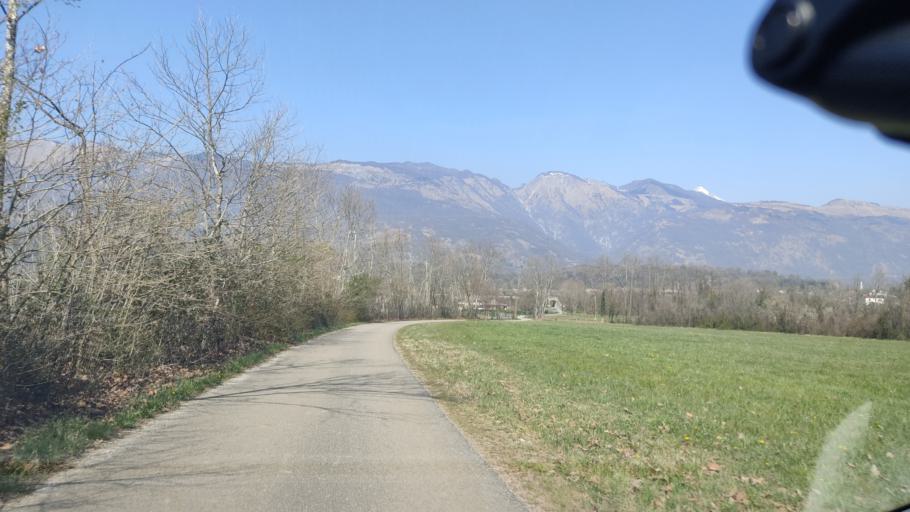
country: IT
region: Friuli Venezia Giulia
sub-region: Provincia di Pordenone
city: Budoia
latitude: 46.0266
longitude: 12.5357
